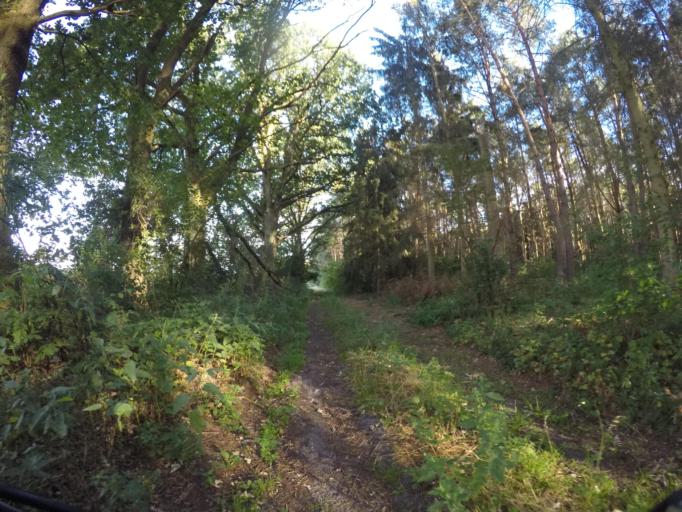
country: DE
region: Lower Saxony
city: Hitzacker
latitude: 53.2249
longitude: 11.0522
